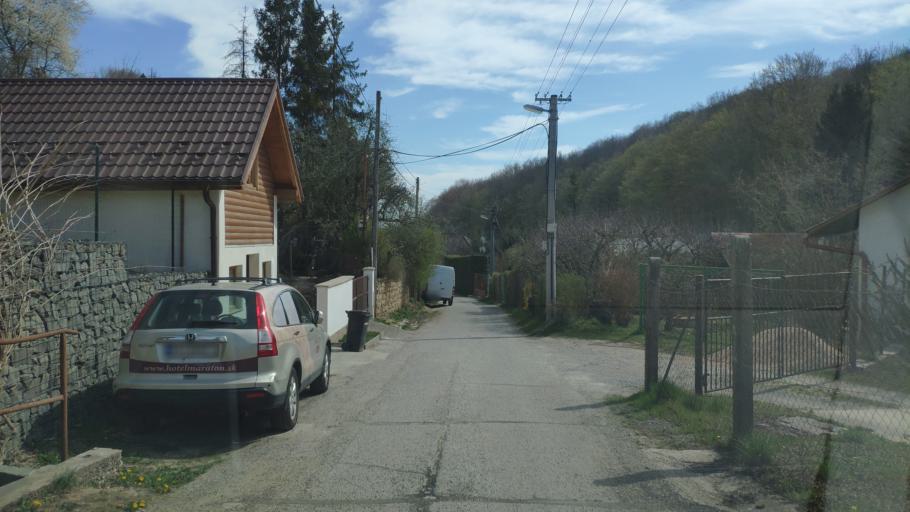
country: SK
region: Kosicky
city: Kosice
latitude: 48.7228
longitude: 21.1918
